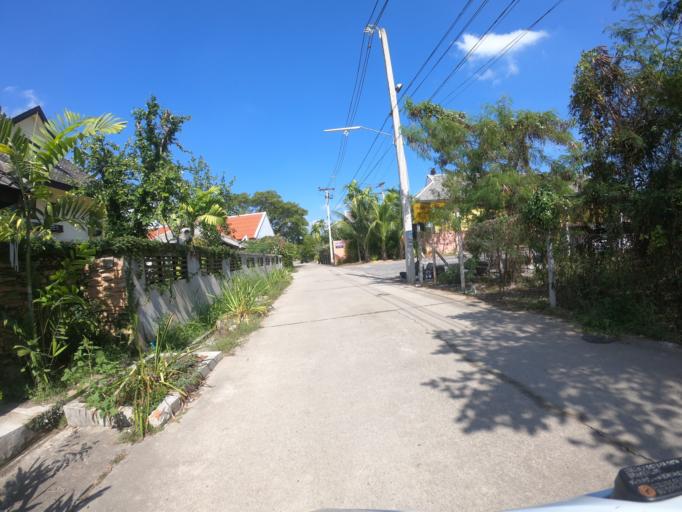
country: TH
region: Chiang Mai
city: Chiang Mai
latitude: 18.7426
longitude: 98.9496
